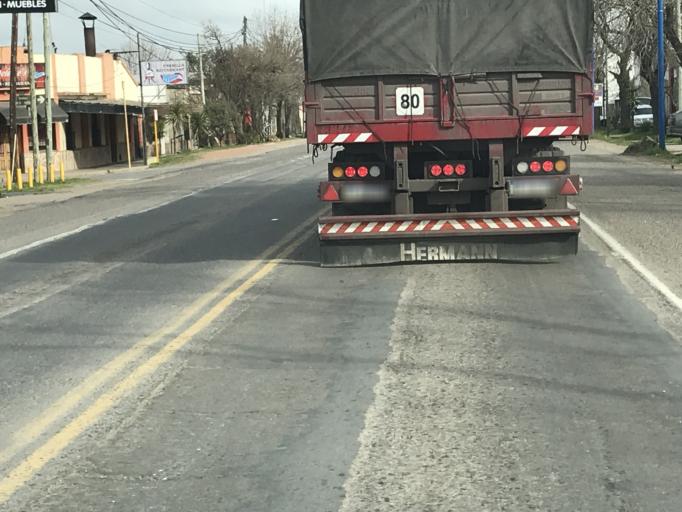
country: AR
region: Santa Fe
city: Canada de Gomez
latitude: -32.8115
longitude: -61.3877
